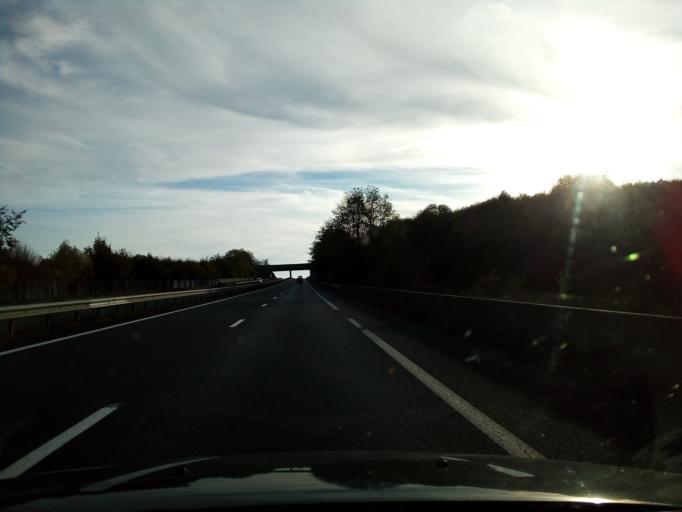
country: FR
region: Poitou-Charentes
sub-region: Departement de la Charente
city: Taponnat-Fleurignac
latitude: 45.7727
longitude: 0.4016
